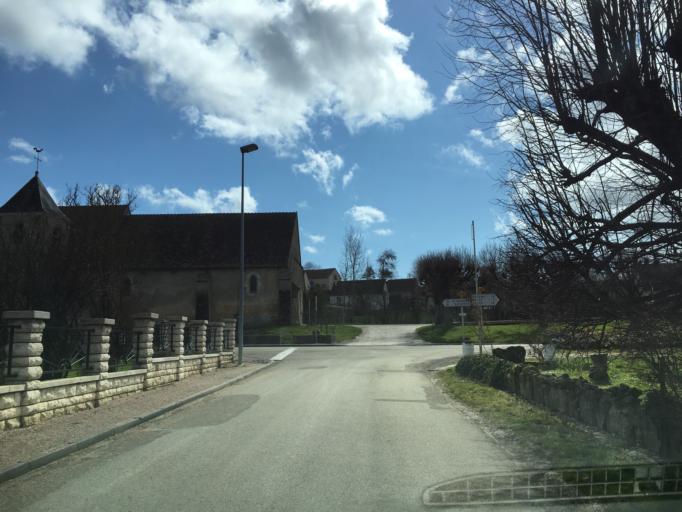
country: FR
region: Bourgogne
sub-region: Departement de l'Yonne
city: Pourrain
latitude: 47.8009
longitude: 3.4180
